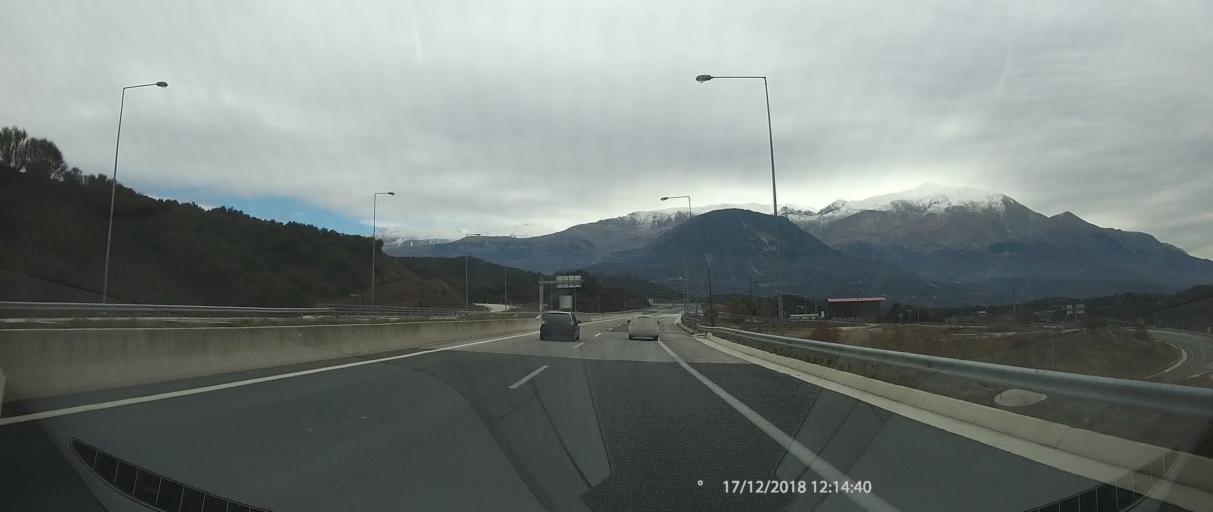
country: GR
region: Epirus
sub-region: Nomos Ioanninon
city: Katsikas
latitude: 39.7177
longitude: 21.0032
